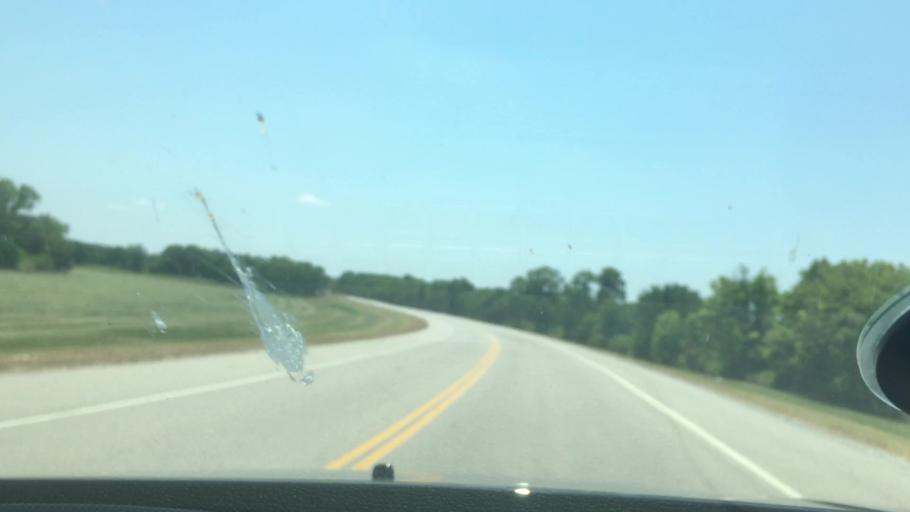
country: US
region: Oklahoma
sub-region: Coal County
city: Coalgate
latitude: 34.5418
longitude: -96.4083
